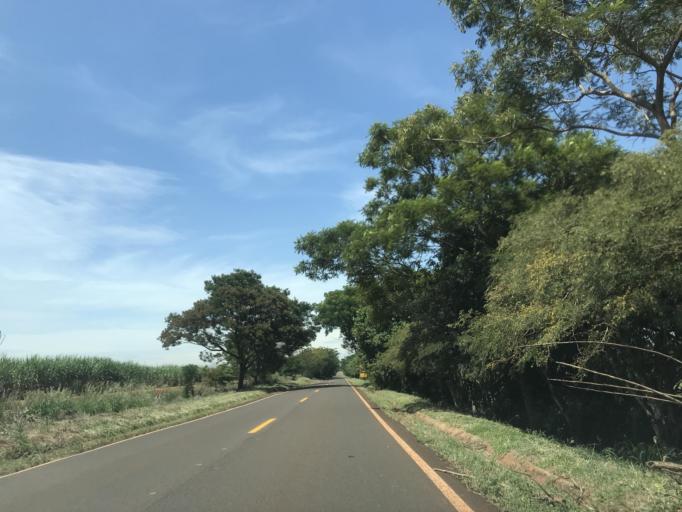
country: BR
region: Parana
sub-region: Paranavai
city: Nova Aurora
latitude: -22.8095
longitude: -52.6542
